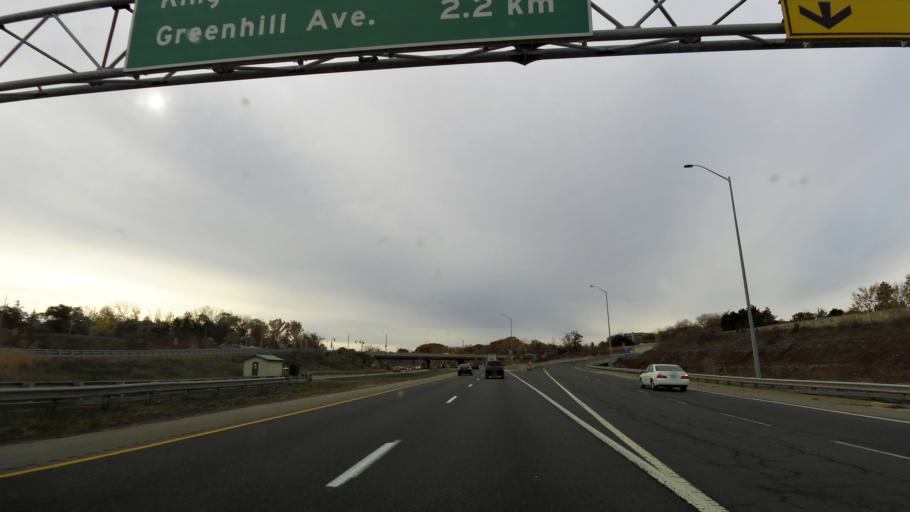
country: CA
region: Ontario
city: Hamilton
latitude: 43.2336
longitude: -79.7815
